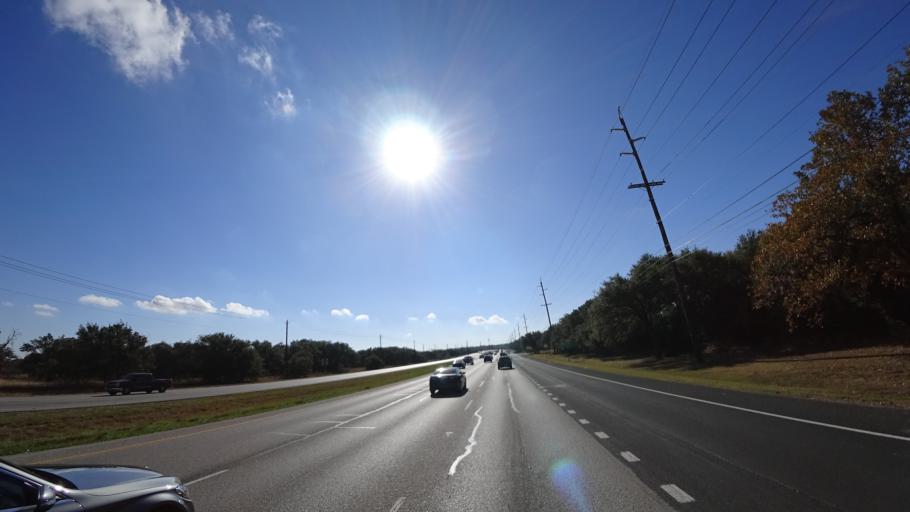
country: US
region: Texas
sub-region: Williamson County
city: Jollyville
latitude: 30.4733
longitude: -97.7637
